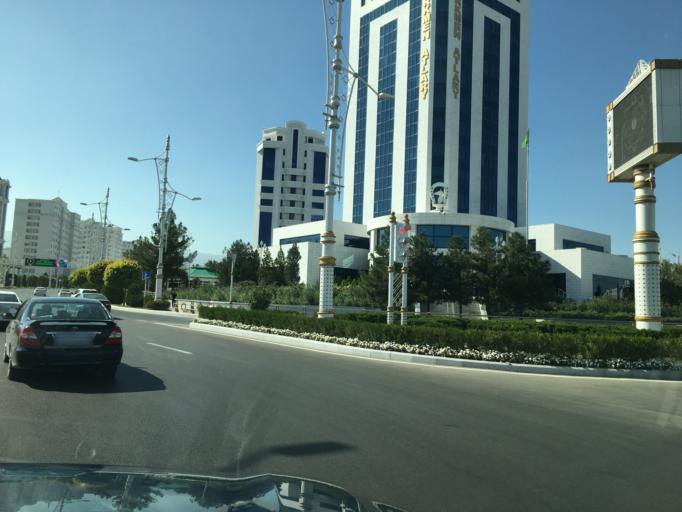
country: TM
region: Ahal
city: Ashgabat
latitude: 37.9271
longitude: 58.3721
